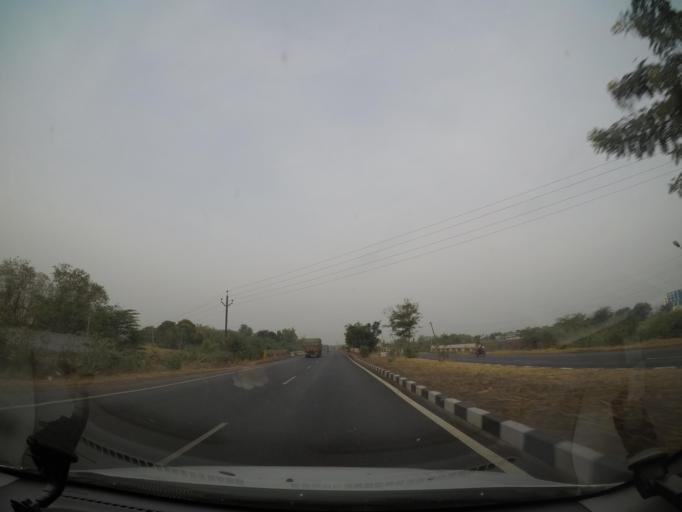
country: IN
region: Andhra Pradesh
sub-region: Krishna
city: Gannavaram
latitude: 16.6216
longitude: 80.9328
